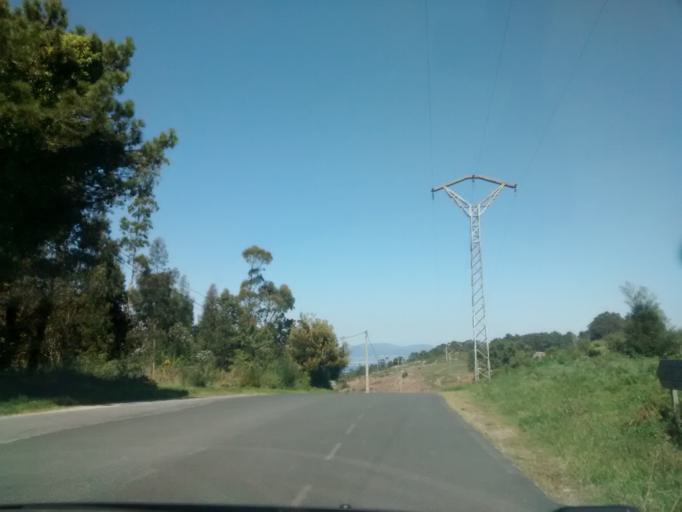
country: ES
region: Galicia
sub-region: Provincia de Pontevedra
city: O Grove
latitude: 42.4757
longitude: -8.8812
